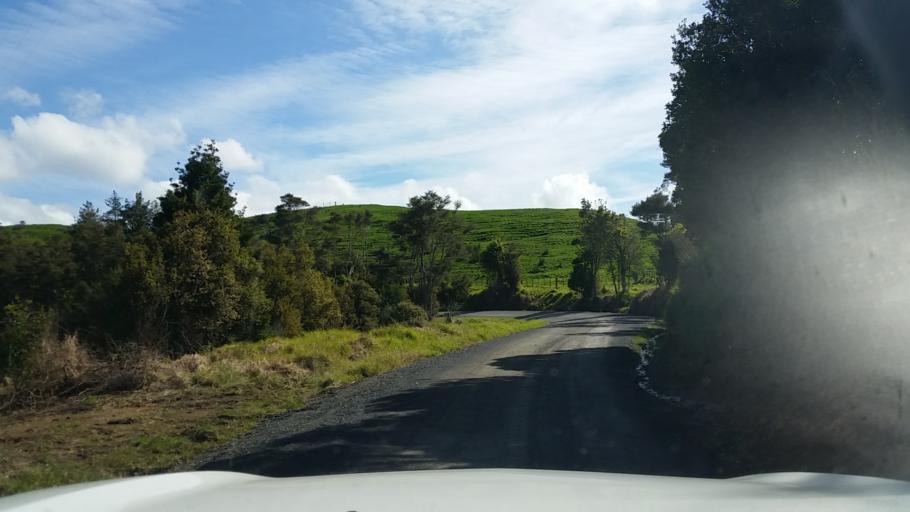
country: NZ
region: Waikato
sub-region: Hauraki District
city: Ngatea
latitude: -37.4479
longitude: 175.4791
